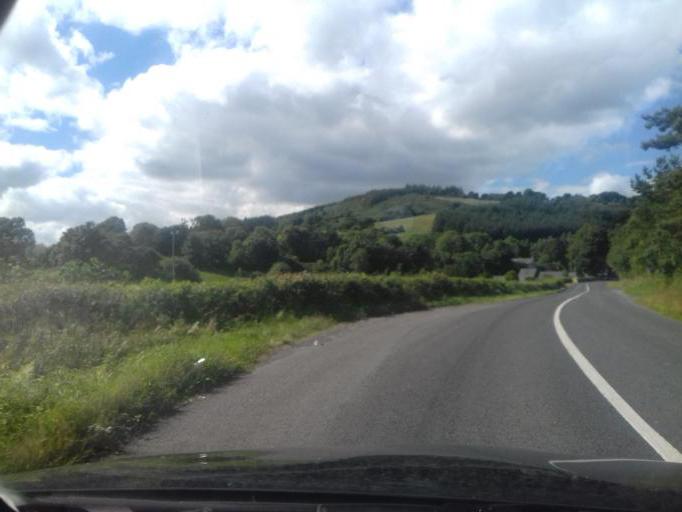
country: IE
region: Munster
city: Carrick-on-Suir
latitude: 52.4016
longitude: -7.4802
